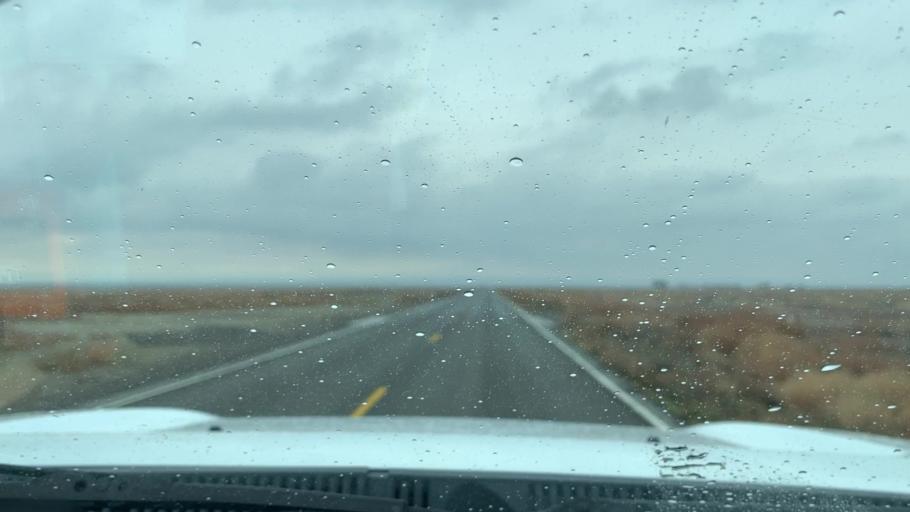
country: US
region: California
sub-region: Kings County
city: Kettleman City
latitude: 35.9341
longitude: -119.7894
